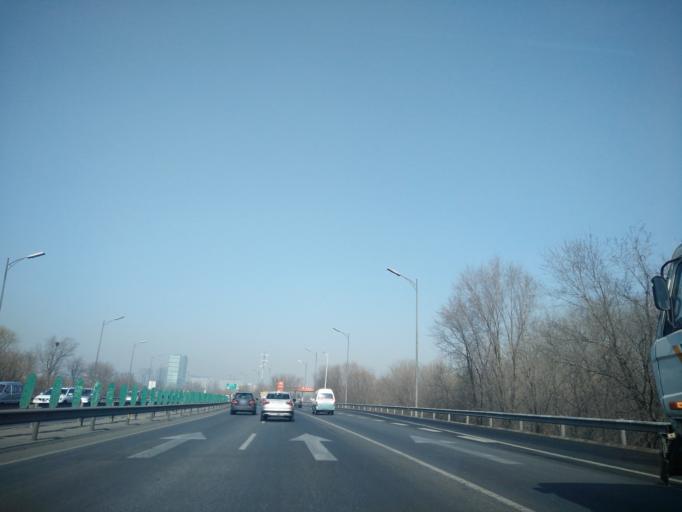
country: CN
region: Beijing
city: Wangjing
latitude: 40.0104
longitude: 116.4816
